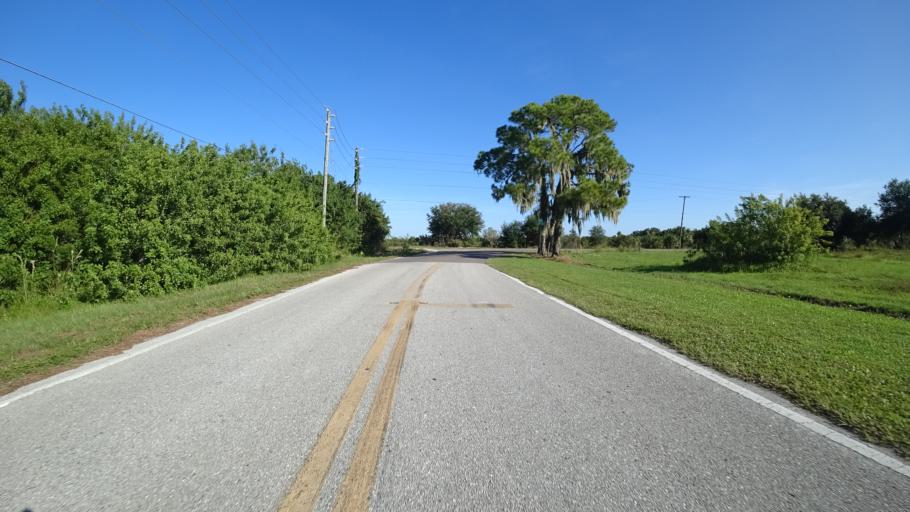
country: US
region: Florida
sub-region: Manatee County
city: Memphis
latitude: 27.6449
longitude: -82.5399
